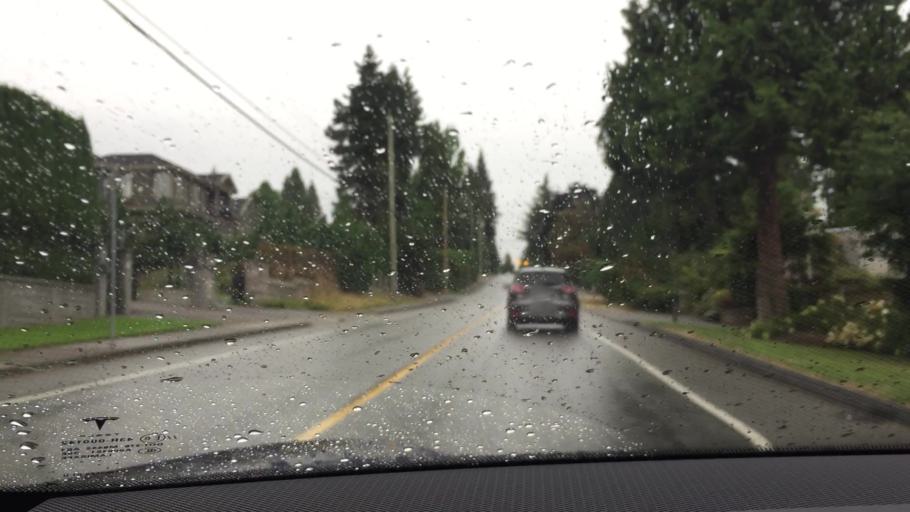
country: CA
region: British Columbia
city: Burnaby
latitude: 49.2318
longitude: -122.9612
